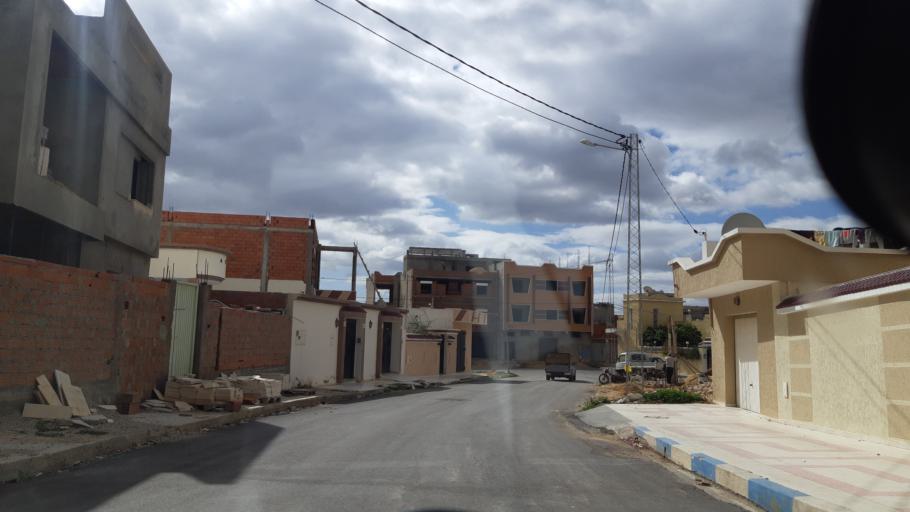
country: TN
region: Susah
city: Akouda
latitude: 35.8702
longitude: 10.5196
